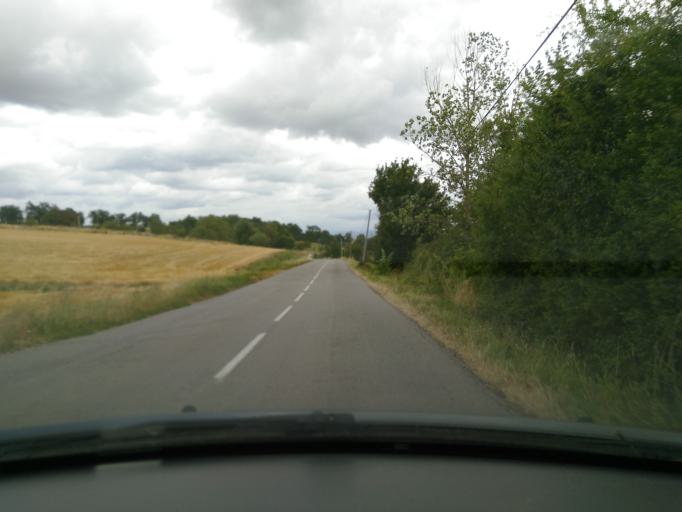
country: FR
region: Rhone-Alpes
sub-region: Departement de l'Isere
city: Beaurepaire
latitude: 45.4051
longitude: 5.1228
